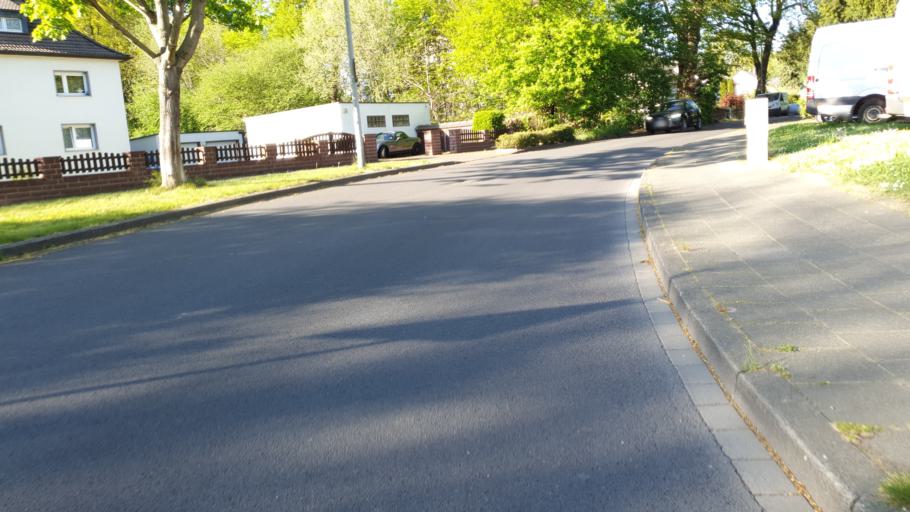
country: DE
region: North Rhine-Westphalia
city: Opladen
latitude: 51.0498
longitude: 7.0543
